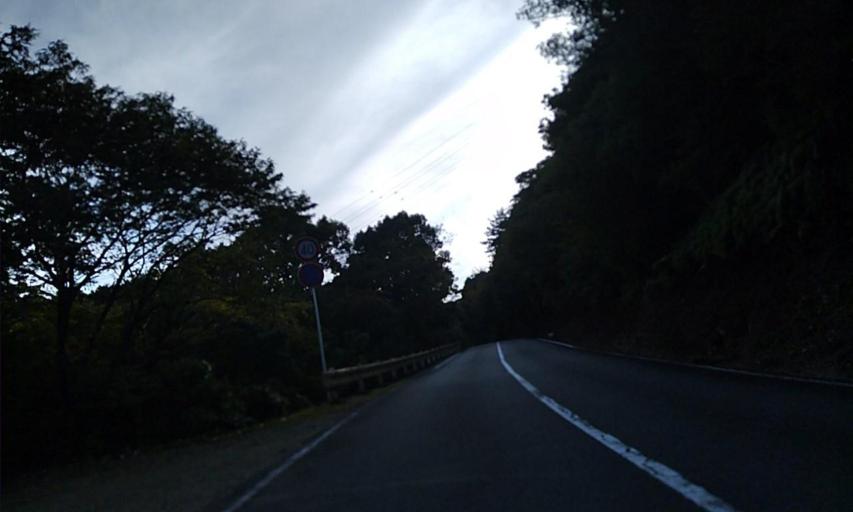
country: JP
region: Mie
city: Toba
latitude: 34.4704
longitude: 136.8282
